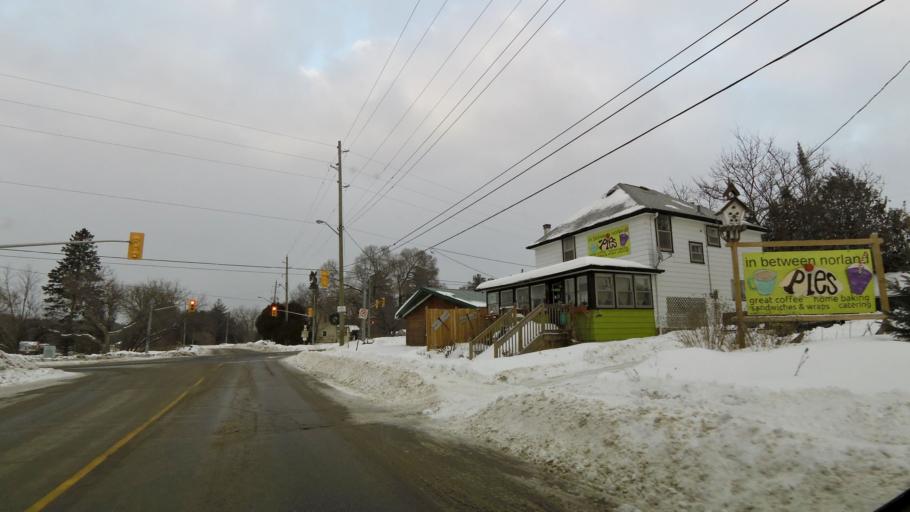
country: CA
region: Ontario
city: Omemee
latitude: 44.7271
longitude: -78.8120
